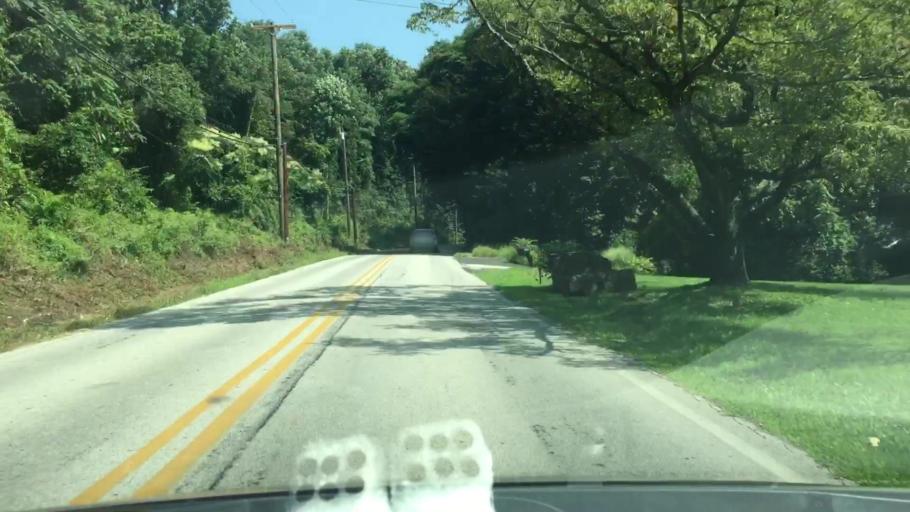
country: US
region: Pennsylvania
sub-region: Delaware County
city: Media
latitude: 39.8933
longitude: -75.3958
